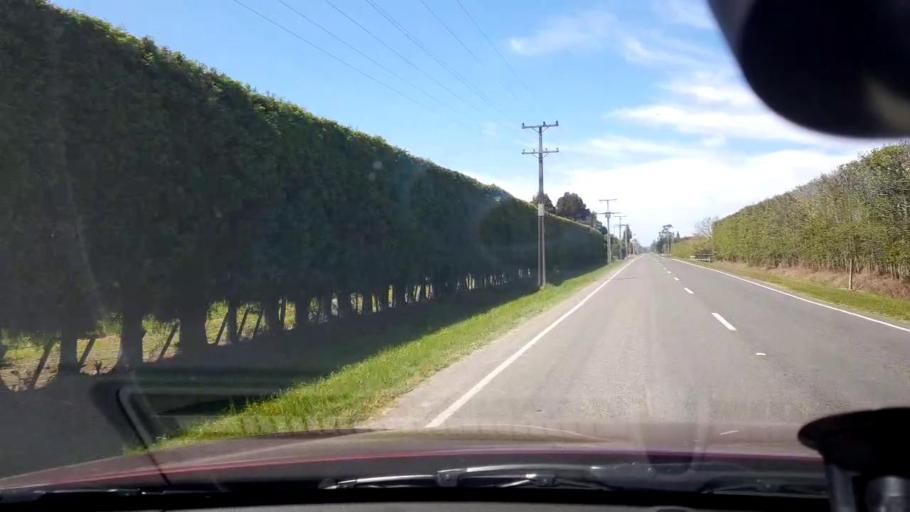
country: NZ
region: Gisborne
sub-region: Gisborne District
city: Gisborne
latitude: -38.6392
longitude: 177.9332
